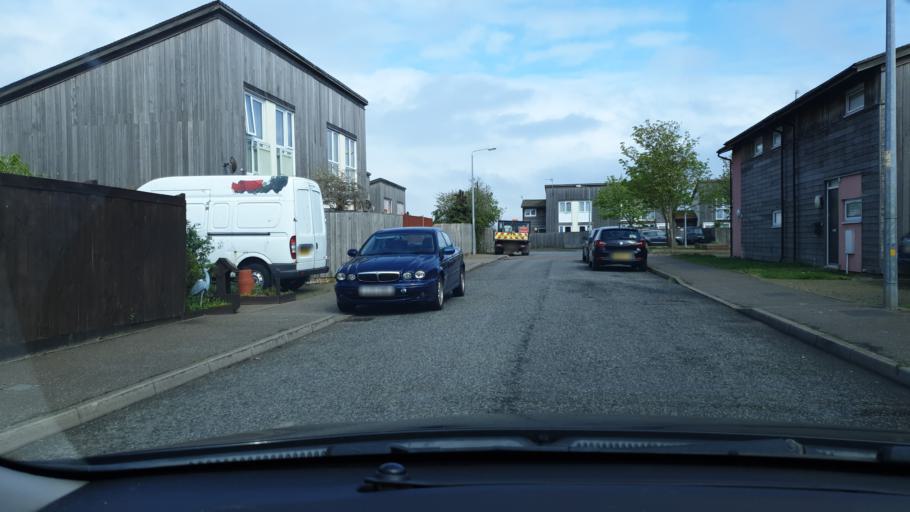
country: GB
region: England
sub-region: Essex
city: Saint Osyth
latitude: 51.7750
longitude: 1.1063
